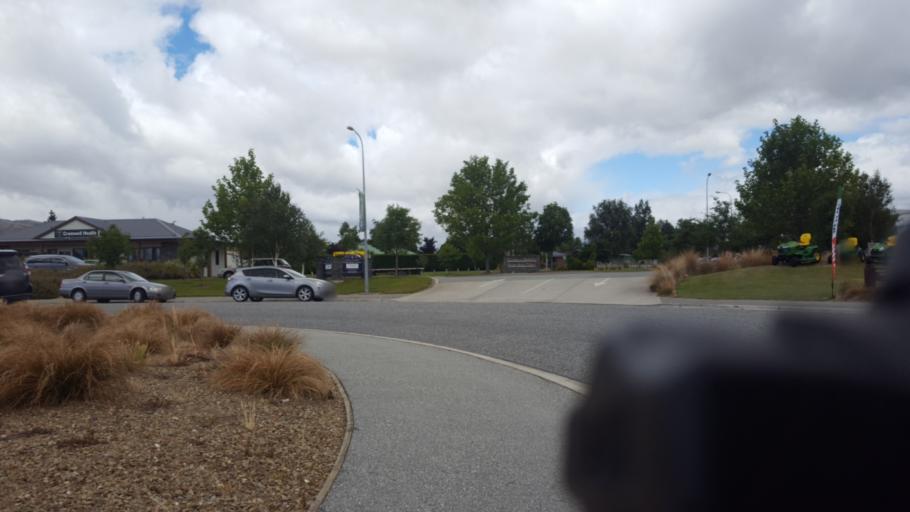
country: NZ
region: Otago
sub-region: Queenstown-Lakes District
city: Wanaka
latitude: -45.0367
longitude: 169.1926
